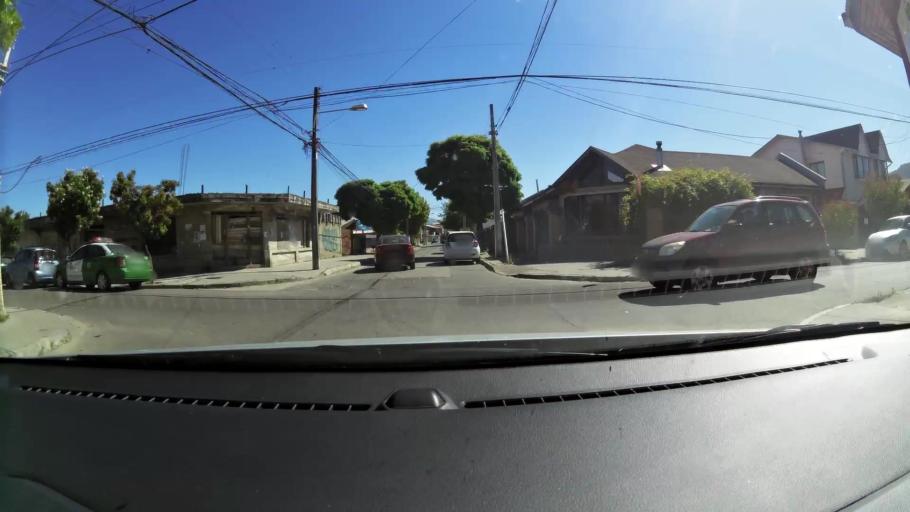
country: CL
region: Valparaiso
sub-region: Provincia de Marga Marga
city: Quilpue
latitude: -33.3192
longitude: -71.4076
